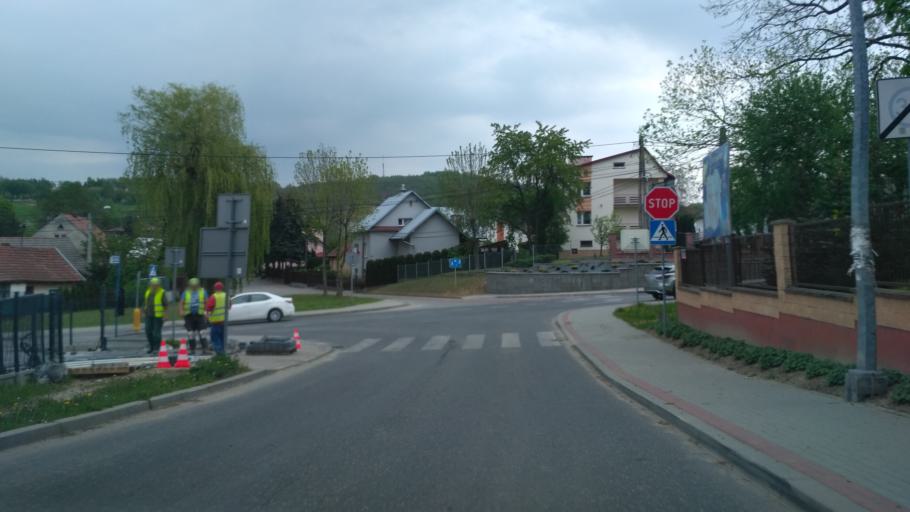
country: PL
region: Lesser Poland Voivodeship
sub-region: Powiat tarnowski
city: Tarnowiec
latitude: 49.9838
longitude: 20.9847
